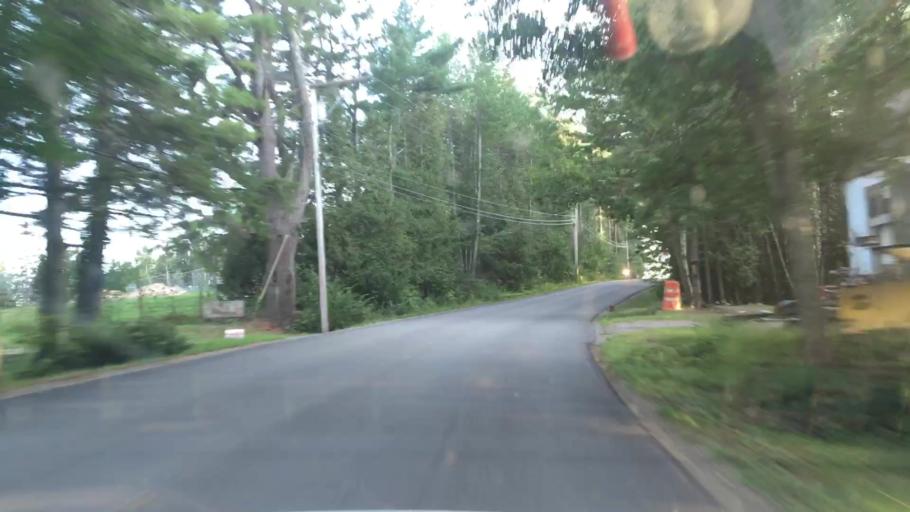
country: US
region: Maine
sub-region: Penobscot County
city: Hampden
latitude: 44.7118
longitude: -68.8869
